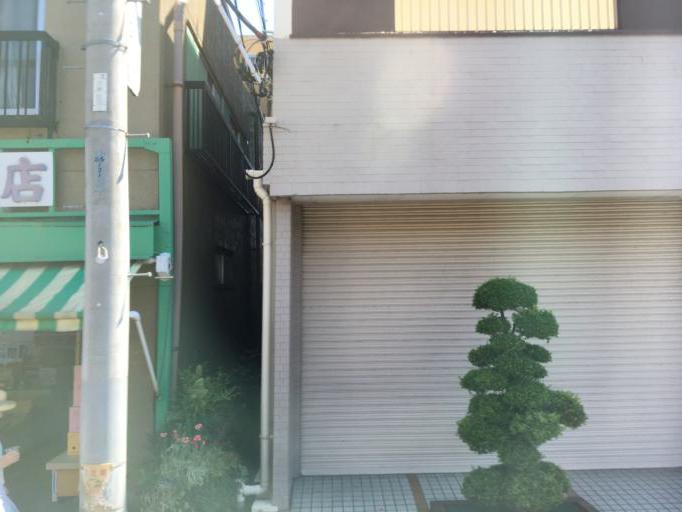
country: JP
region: Saitama
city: Kawagoe
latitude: 35.9286
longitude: 139.4830
